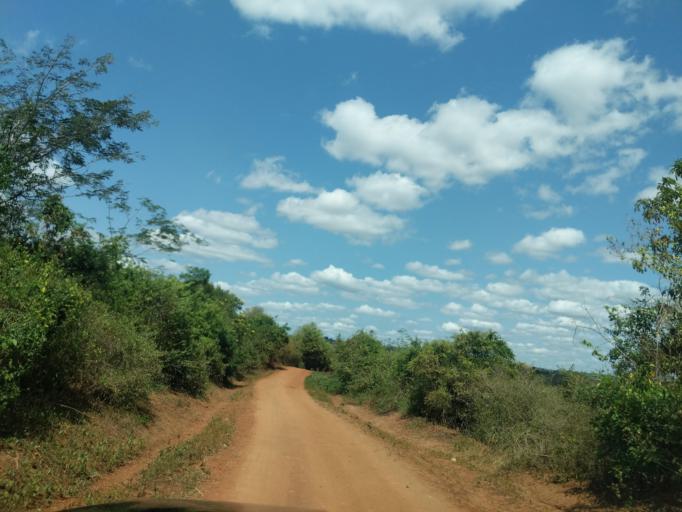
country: TZ
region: Tanga
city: Chanika
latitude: -5.5130
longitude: 38.3639
